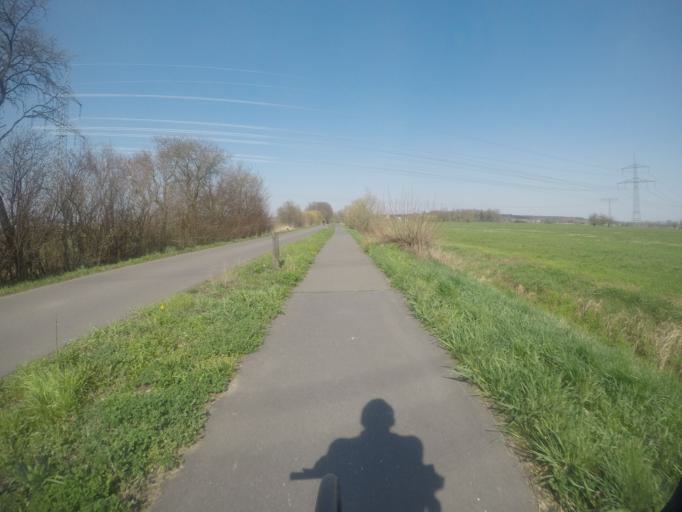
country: DE
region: Brandenburg
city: Falkensee
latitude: 52.6316
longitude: 13.0879
